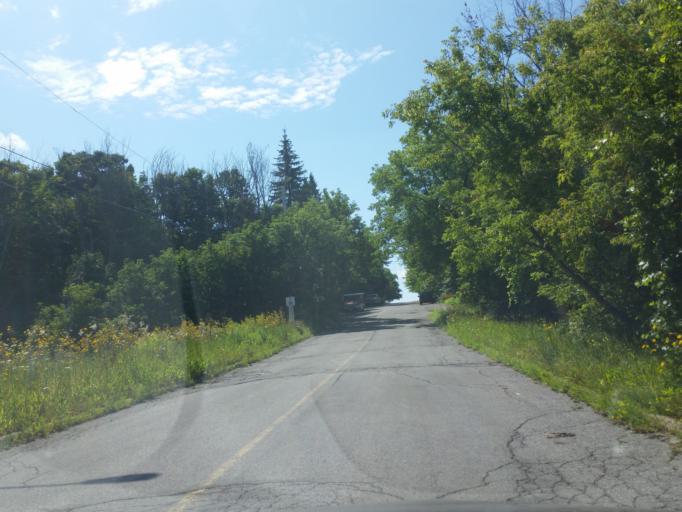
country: CA
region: Quebec
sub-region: Outaouais
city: Gatineau
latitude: 45.4497
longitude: -75.6332
